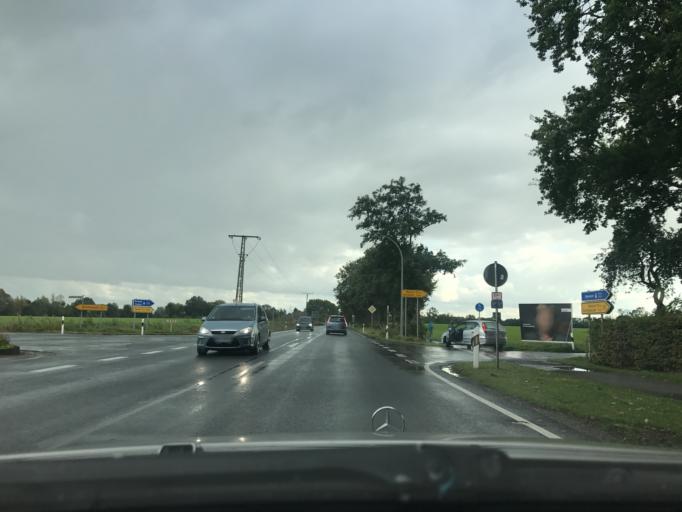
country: DE
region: North Rhine-Westphalia
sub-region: Regierungsbezirk Arnsberg
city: Soest
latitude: 51.6301
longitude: 8.0997
